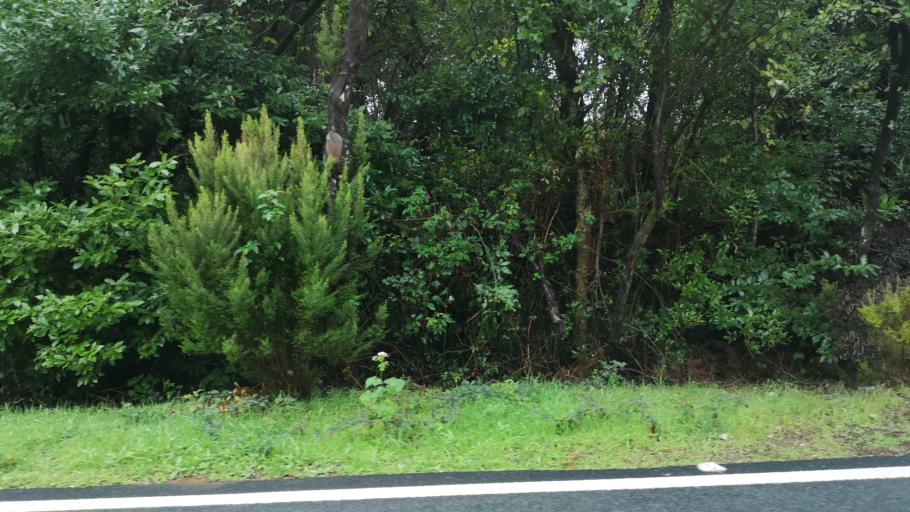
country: ES
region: Canary Islands
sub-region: Provincia de Santa Cruz de Tenerife
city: Vallehermosa
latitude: 28.1235
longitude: -17.2516
